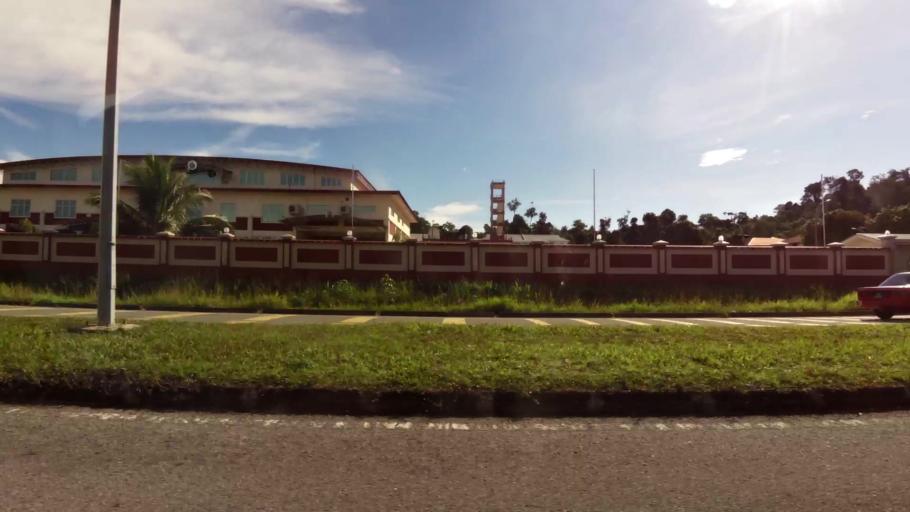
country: BN
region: Brunei and Muara
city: Bandar Seri Begawan
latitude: 4.9731
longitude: 114.9656
